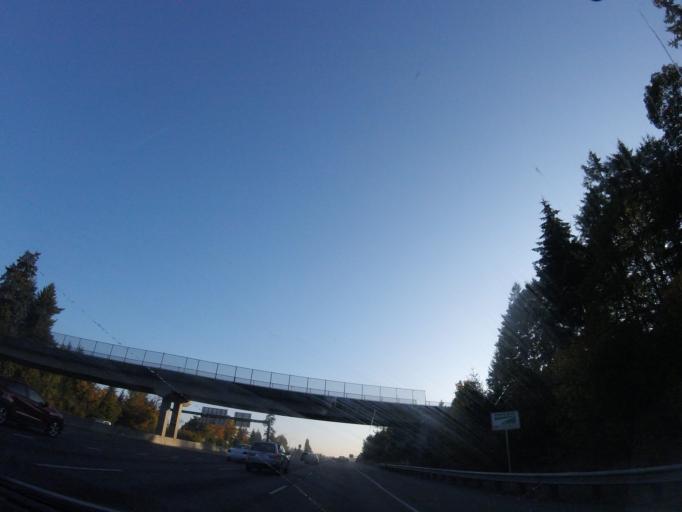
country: US
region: Washington
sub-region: King County
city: Kirkland
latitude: 47.6913
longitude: -122.1821
